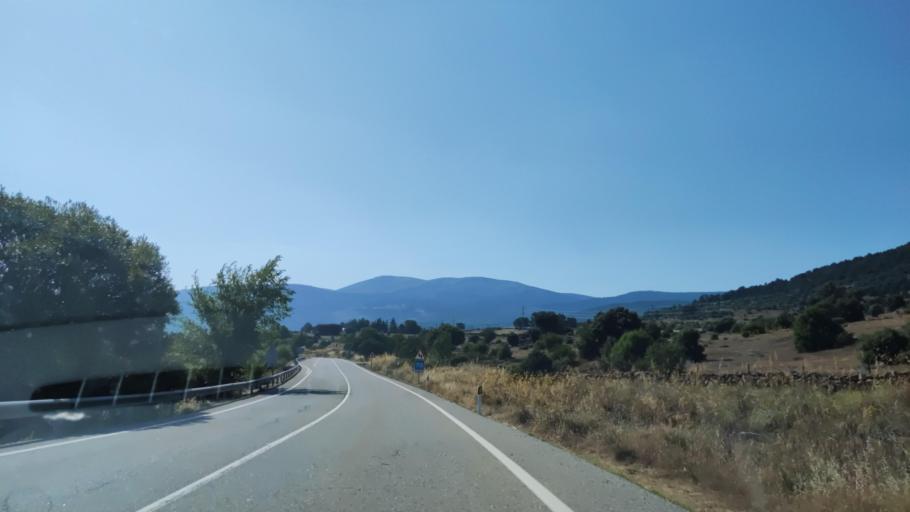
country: ES
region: Madrid
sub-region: Provincia de Madrid
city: Lozoya
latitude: 40.9471
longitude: -3.7614
